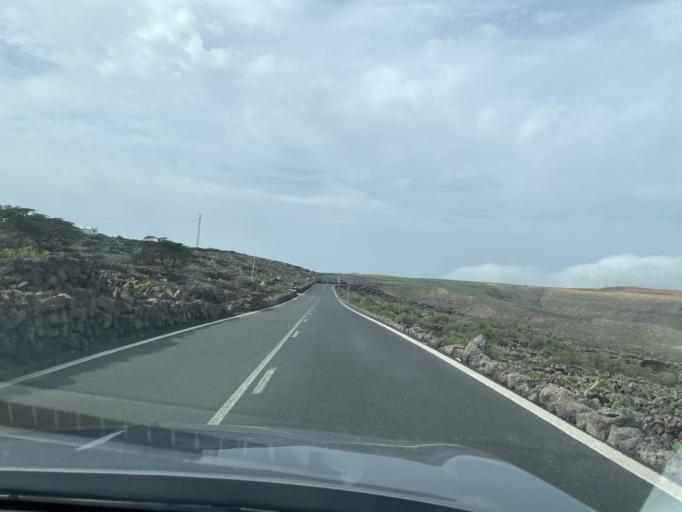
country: ES
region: Canary Islands
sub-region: Provincia de Las Palmas
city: Haria
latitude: 29.1934
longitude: -13.4739
